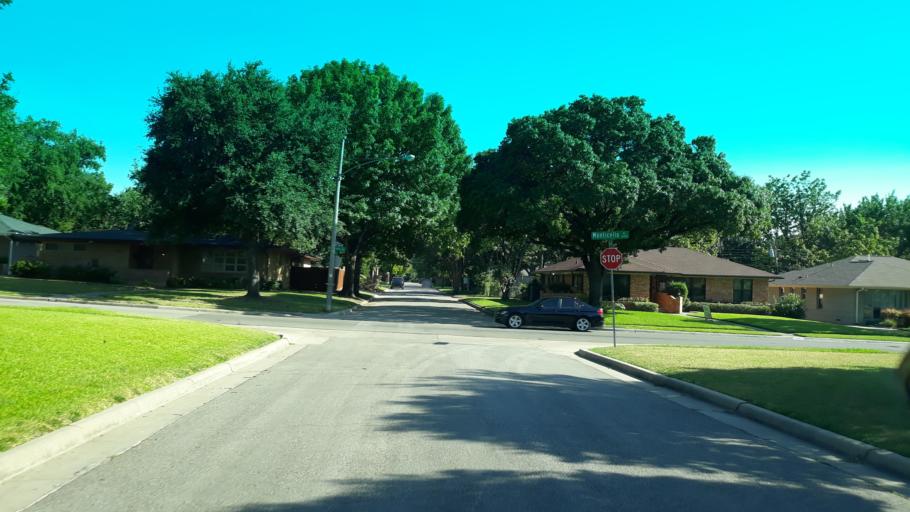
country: US
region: Texas
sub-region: Dallas County
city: Highland Park
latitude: 32.8269
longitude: -96.7581
